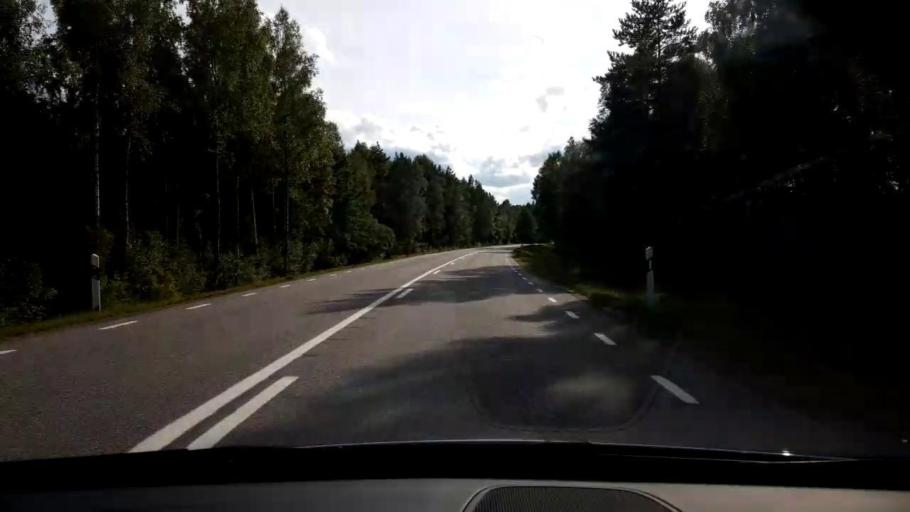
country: SE
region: Joenkoeping
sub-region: Savsjo Kommun
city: Vrigstad
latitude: 57.2923
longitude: 14.2971
